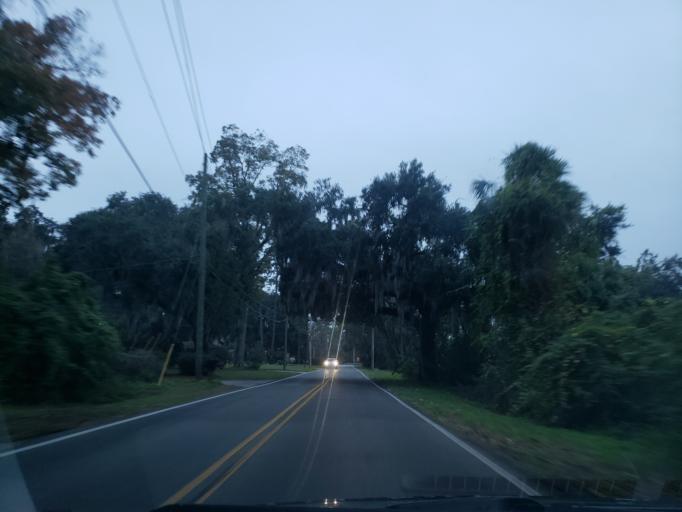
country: US
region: Georgia
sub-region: Chatham County
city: Isle of Hope
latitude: 32.0029
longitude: -81.0635
